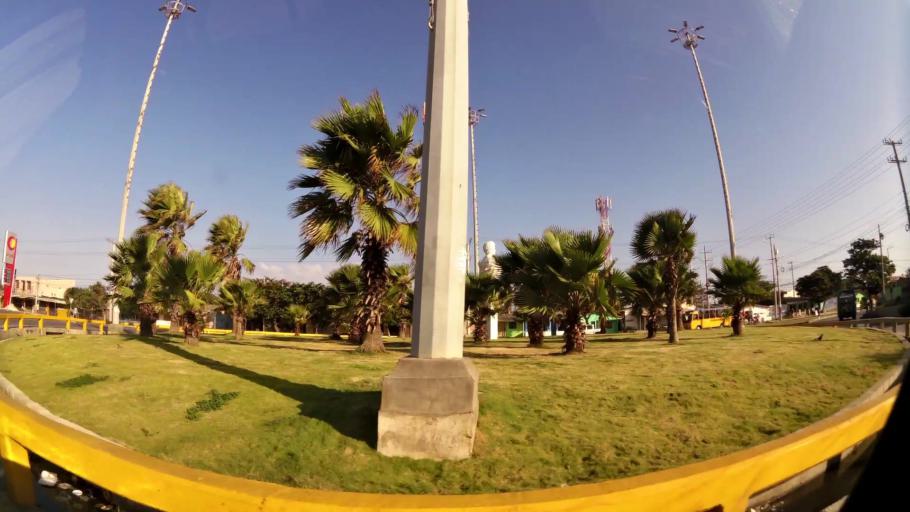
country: CO
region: Atlantico
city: Barranquilla
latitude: 11.0384
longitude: -74.8269
